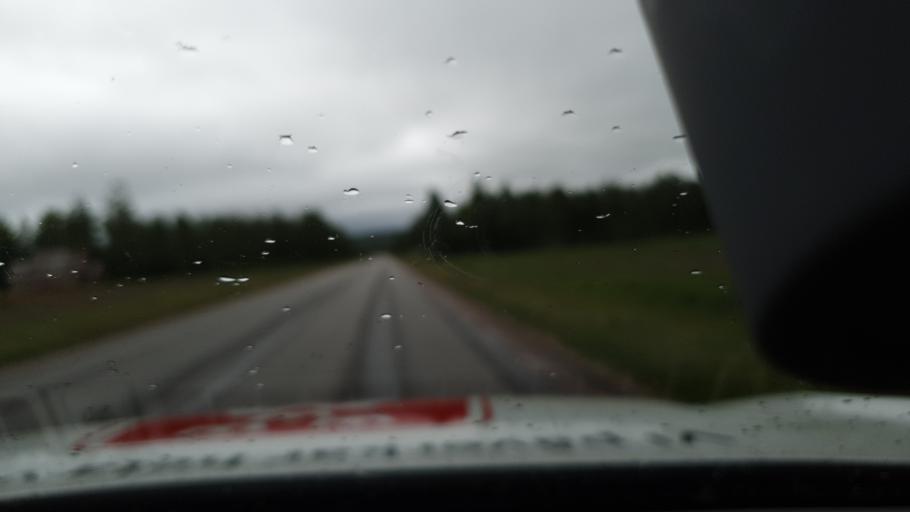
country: SE
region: Norrbotten
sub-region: Overtornea Kommun
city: OEvertornea
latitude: 66.4097
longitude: 23.6239
